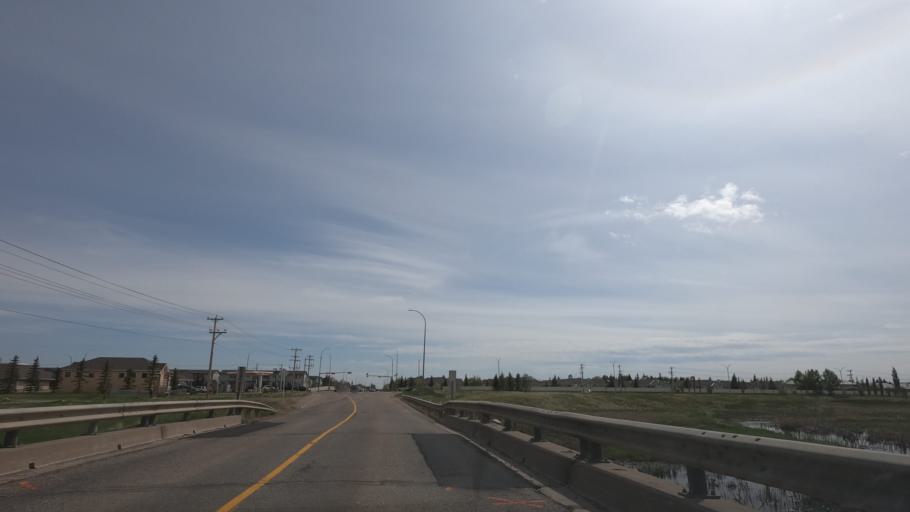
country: CA
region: Alberta
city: Airdrie
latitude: 51.3017
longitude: -114.0253
